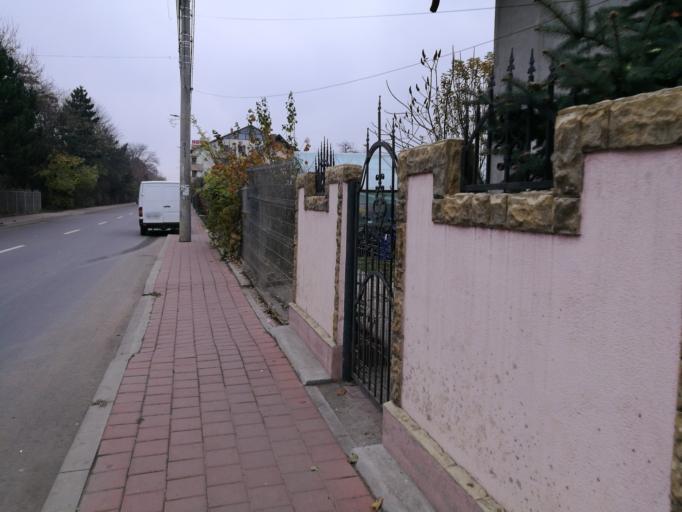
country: RO
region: Suceava
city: Suceava
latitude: 47.6695
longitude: 26.2710
